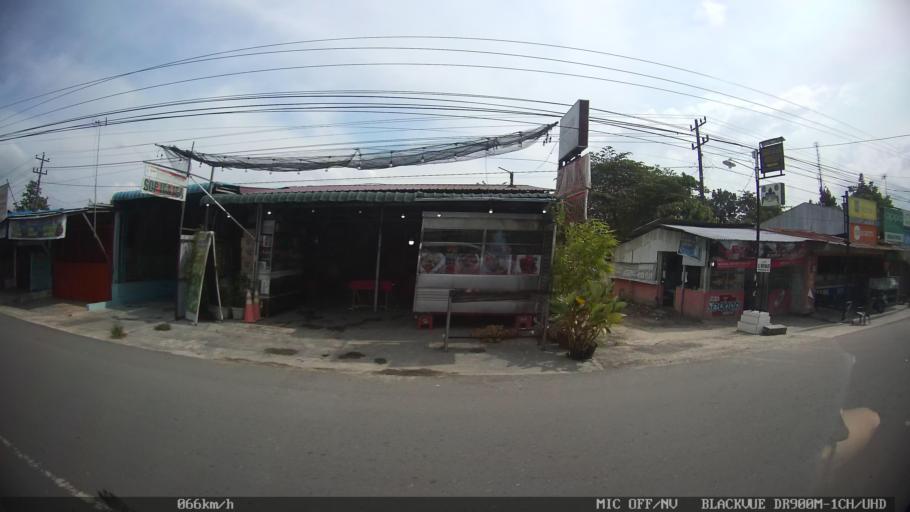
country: ID
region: North Sumatra
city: Percut
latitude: 3.6122
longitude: 98.8061
